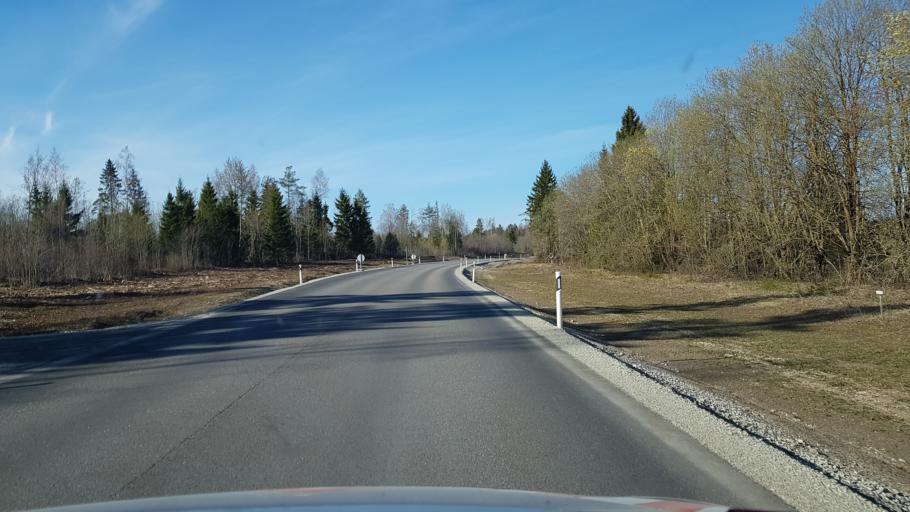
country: EE
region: Laeaene-Virumaa
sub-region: Vinni vald
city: Vinni
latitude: 59.1157
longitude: 26.6174
